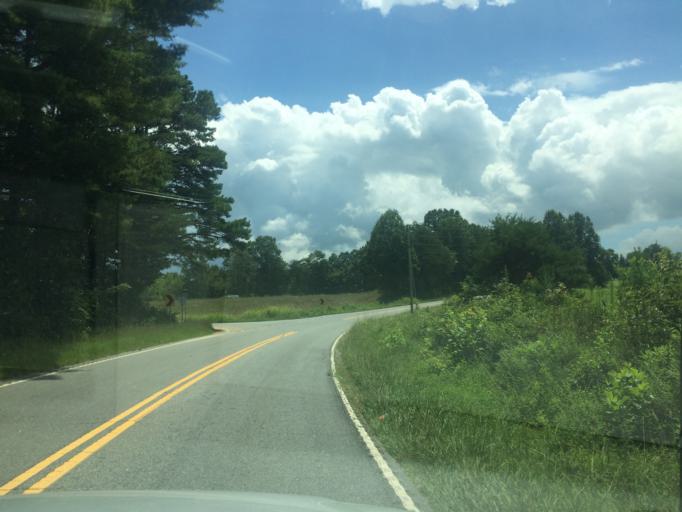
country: US
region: North Carolina
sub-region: Polk County
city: Columbus
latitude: 35.2707
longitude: -82.1078
